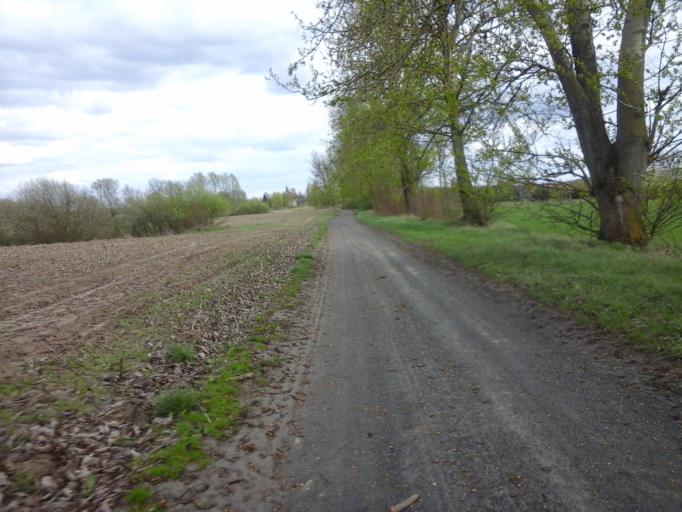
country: PL
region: West Pomeranian Voivodeship
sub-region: Powiat choszczenski
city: Krzecin
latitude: 53.0893
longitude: 15.5402
